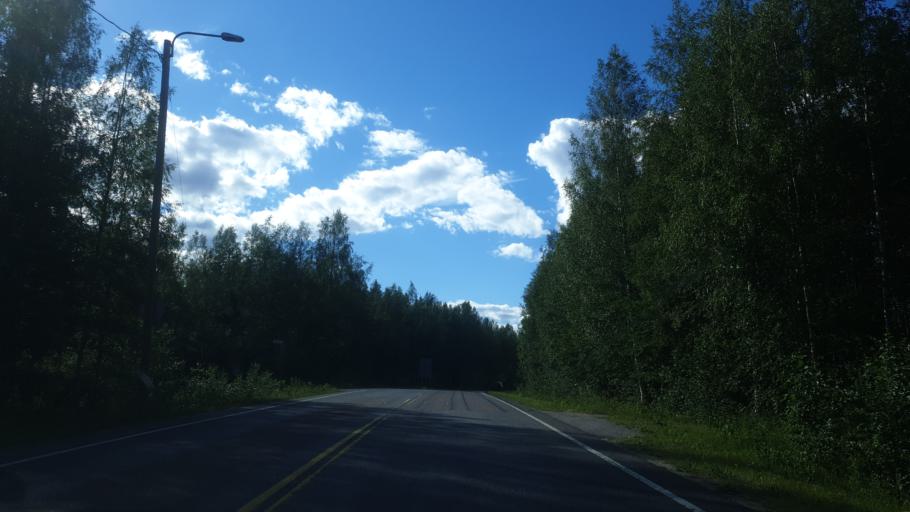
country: FI
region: Southern Savonia
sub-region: Mikkeli
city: Maentyharju
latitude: 61.4803
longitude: 26.7467
